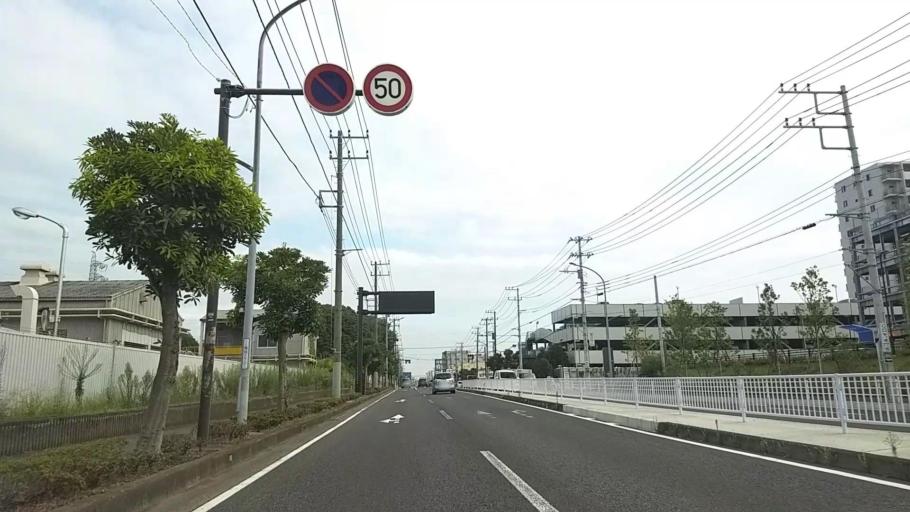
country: JP
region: Kanagawa
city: Hiratsuka
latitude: 35.3371
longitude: 139.3576
